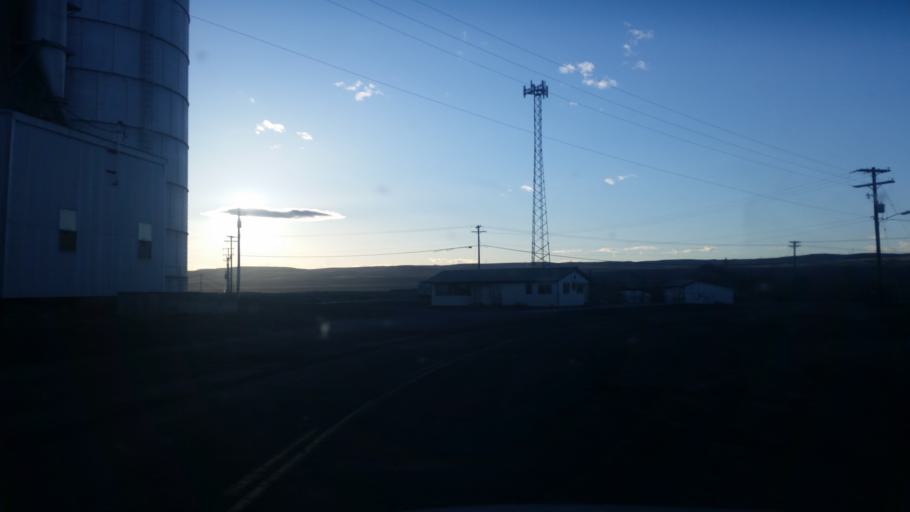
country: US
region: Washington
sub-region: Grant County
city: Soap Lake
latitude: 47.6124
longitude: -119.2978
